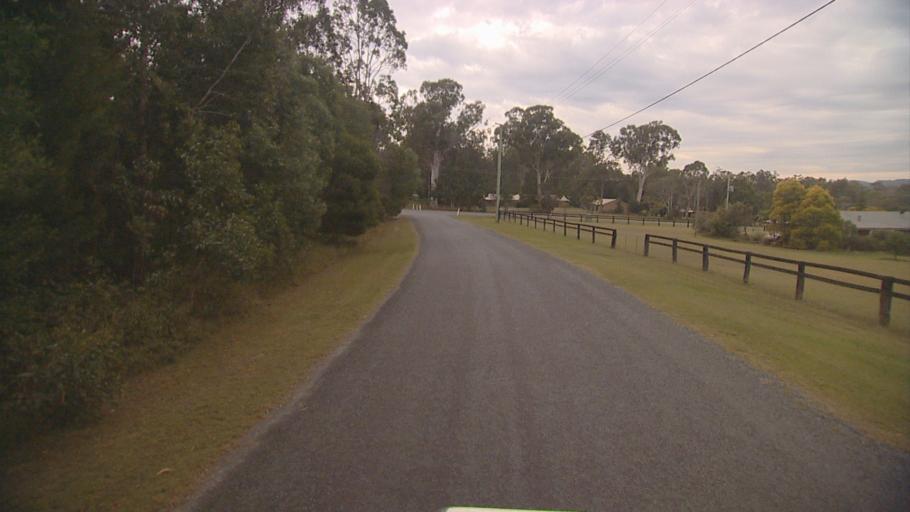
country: AU
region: Queensland
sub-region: Logan
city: Chambers Flat
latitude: -27.7883
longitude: 153.1121
